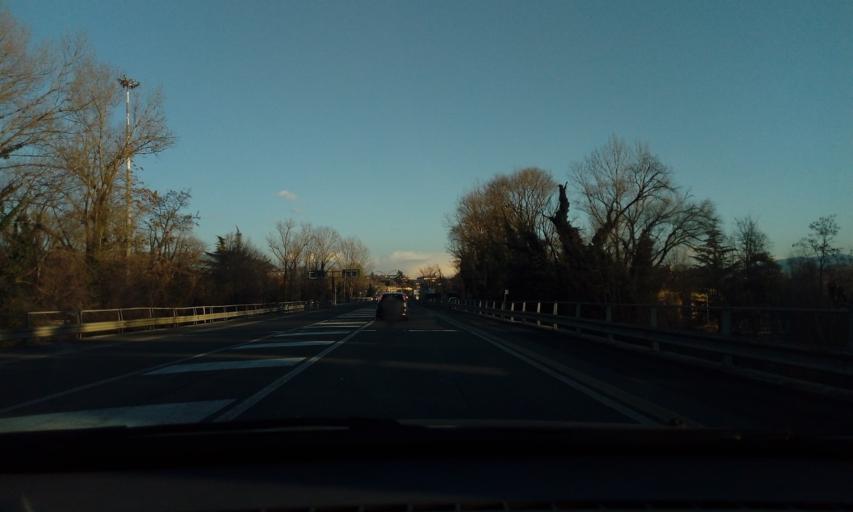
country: IT
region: Friuli Venezia Giulia
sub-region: Provincia di Gorizia
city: Gorizia
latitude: 45.9357
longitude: 13.5948
